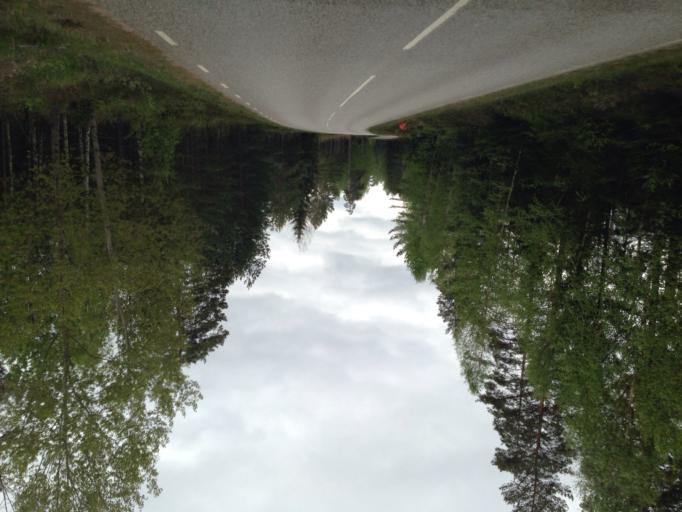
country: SE
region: Soedermanland
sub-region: Eskilstuna Kommun
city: Hallbybrunn
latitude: 59.4027
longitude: 16.3723
